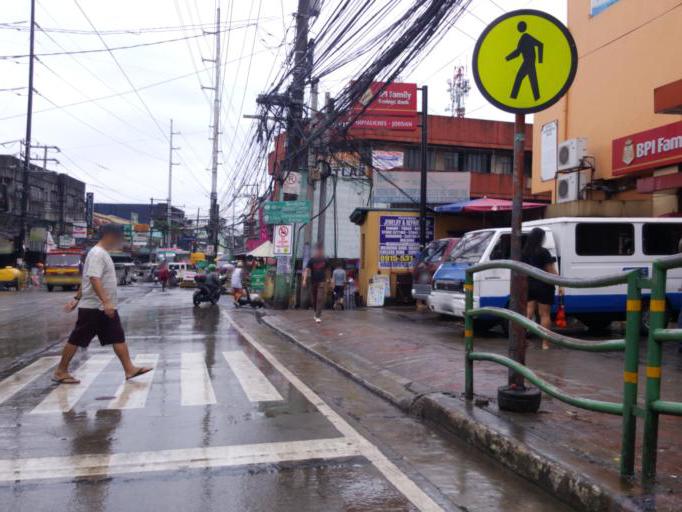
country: PH
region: Calabarzon
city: Bagong Pagasa
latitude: 14.7223
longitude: 121.0416
